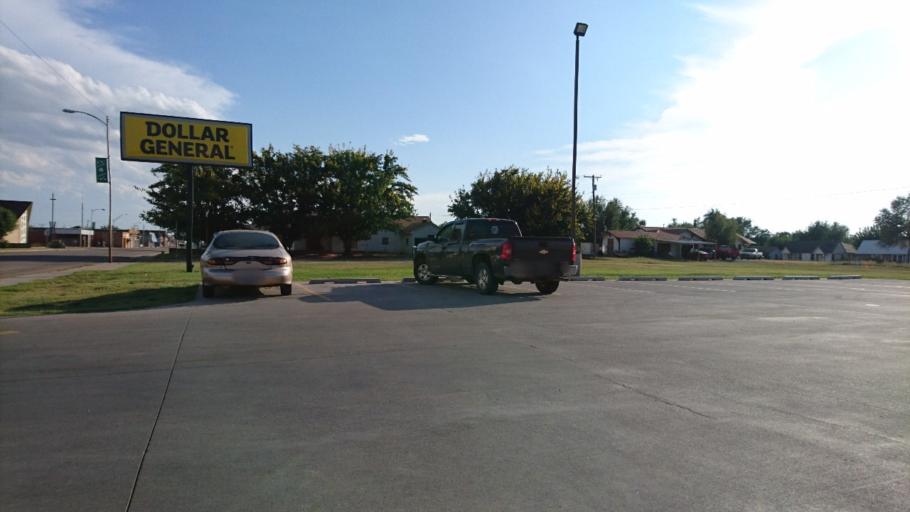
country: US
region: Texas
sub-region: Wheeler County
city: Shamrock
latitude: 35.2201
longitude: -100.2494
